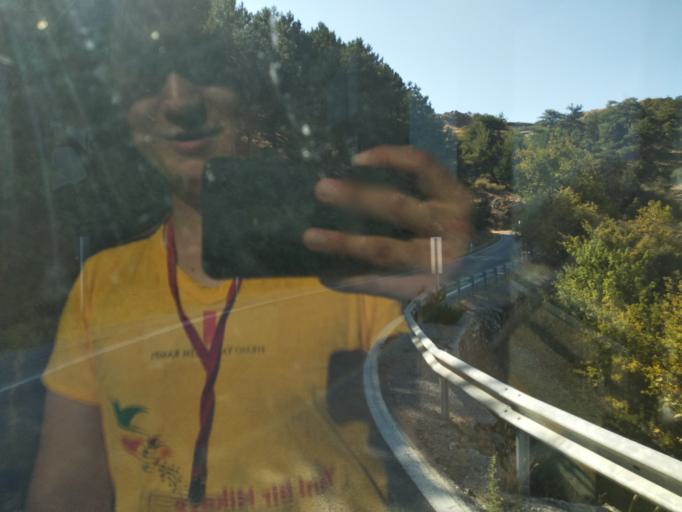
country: TR
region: Izmir
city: Gaziemir
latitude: 38.3214
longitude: 27.0077
